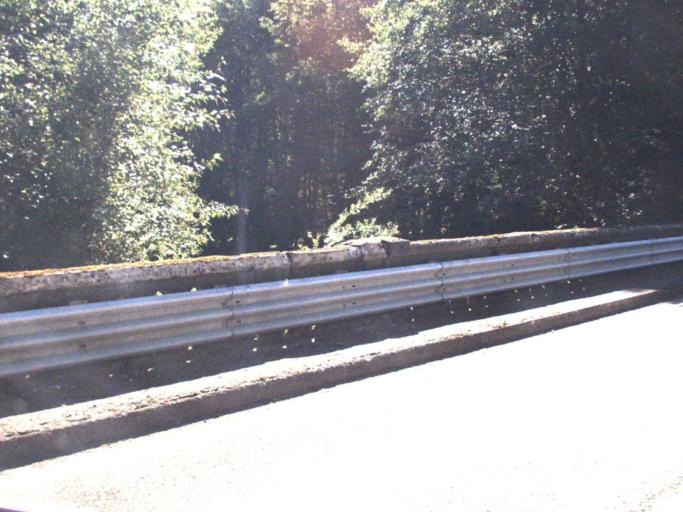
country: US
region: Washington
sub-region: King County
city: Riverbend
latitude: 47.1583
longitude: -121.6581
